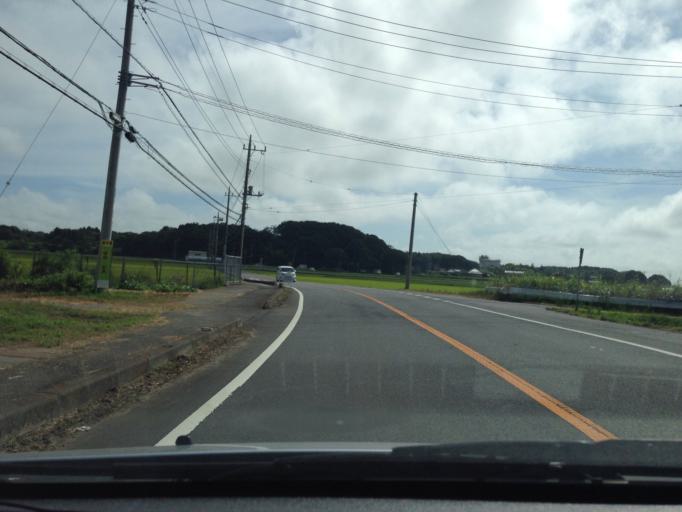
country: JP
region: Ibaraki
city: Inashiki
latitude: 36.0104
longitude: 140.3368
